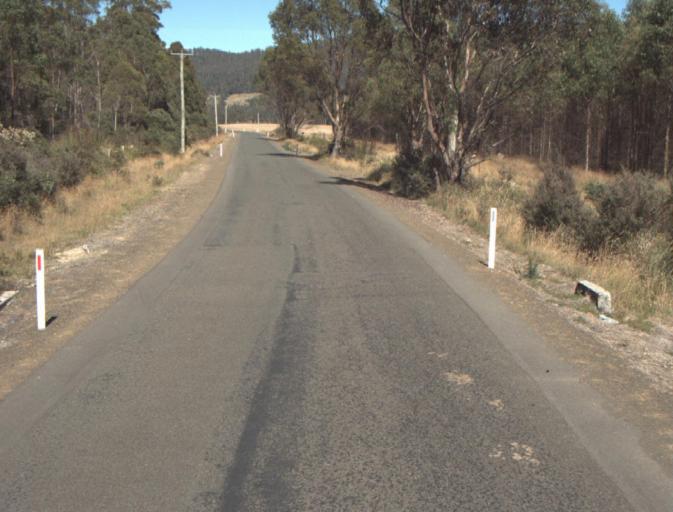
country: AU
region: Tasmania
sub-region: Launceston
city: Newstead
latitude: -41.3266
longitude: 147.3147
